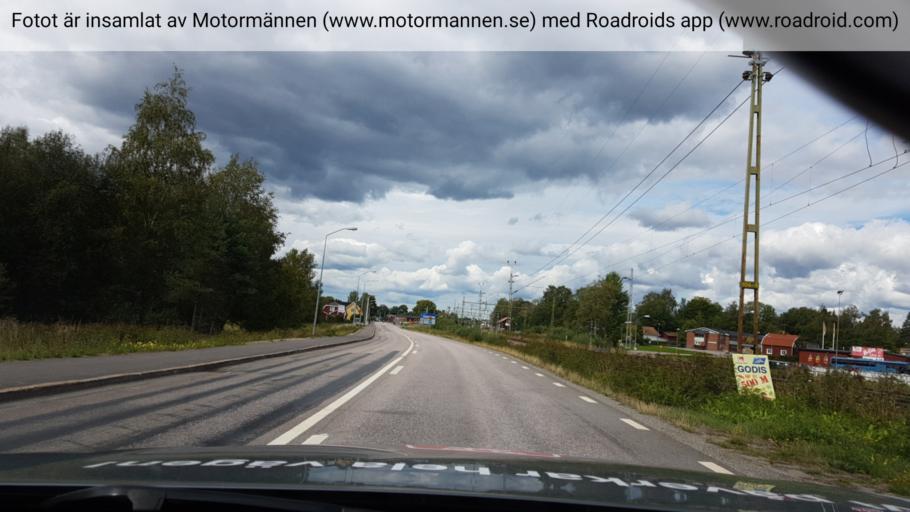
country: SE
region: Uppsala
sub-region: Heby Kommun
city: Morgongava
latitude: 59.9318
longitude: 16.9683
